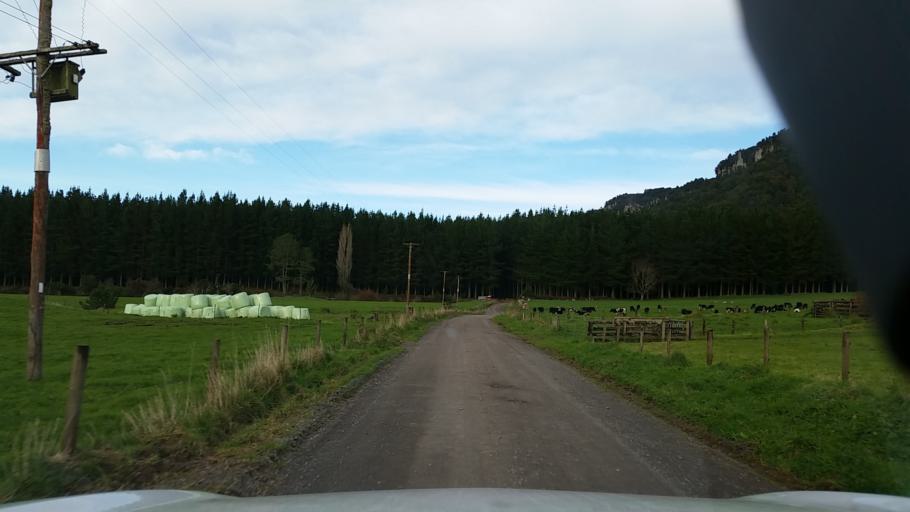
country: NZ
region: Bay of Plenty
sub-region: Rotorua District
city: Rotorua
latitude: -38.2309
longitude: 176.1590
